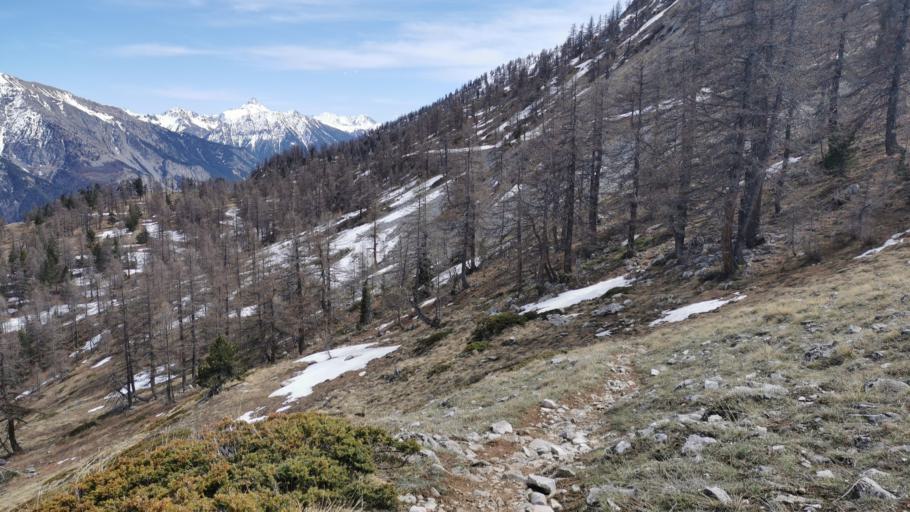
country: FR
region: Provence-Alpes-Cote d'Azur
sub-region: Departement des Hautes-Alpes
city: Saint-Chaffrey
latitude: 44.9960
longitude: 6.6466
